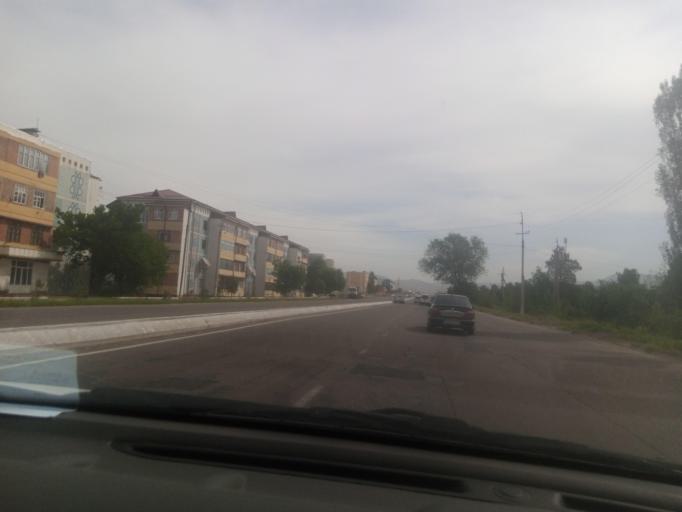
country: UZ
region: Toshkent
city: Angren
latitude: 41.0112
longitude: 70.1001
